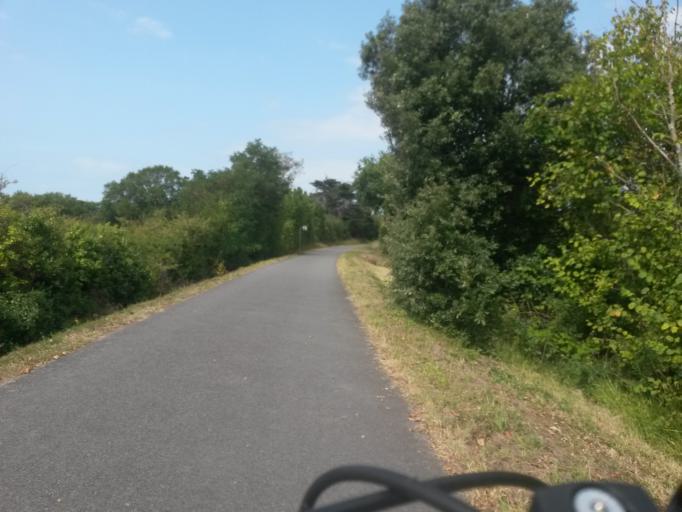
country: FR
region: Pays de la Loire
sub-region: Departement de la Loire-Atlantique
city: Guerande
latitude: 47.3066
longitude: -2.4002
